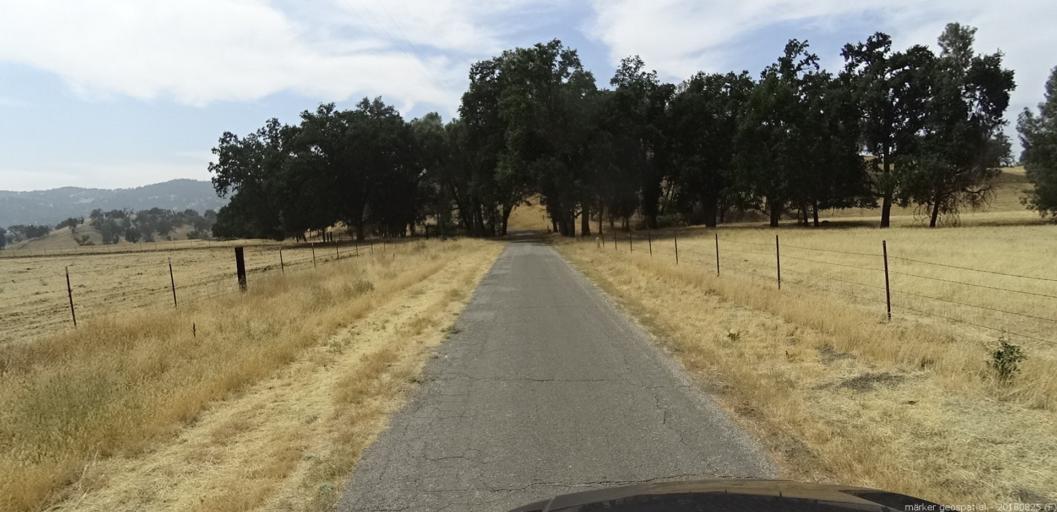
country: US
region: California
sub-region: Fresno County
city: Coalinga
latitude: 36.1835
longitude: -120.6798
